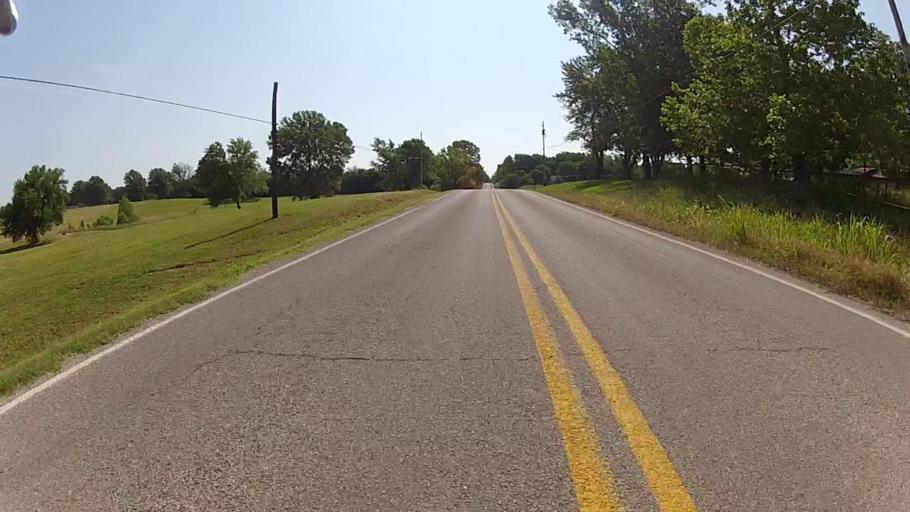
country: US
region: Kansas
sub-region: Montgomery County
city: Independence
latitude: 37.1929
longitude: -95.7181
